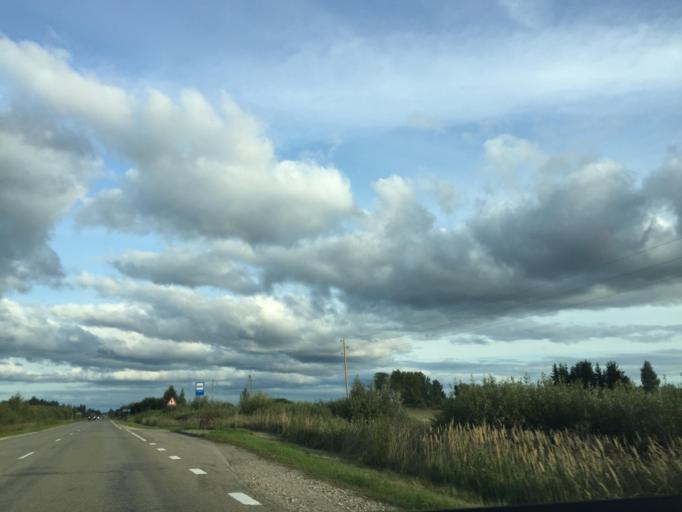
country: LV
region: Nereta
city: Nereta
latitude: 56.2611
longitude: 25.1882
